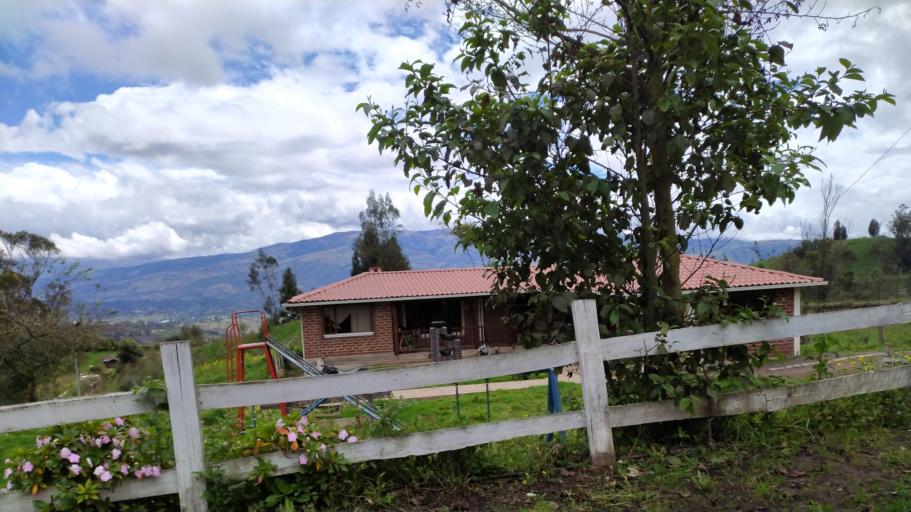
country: EC
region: Chimborazo
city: Riobamba
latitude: -1.6760
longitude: -78.5699
